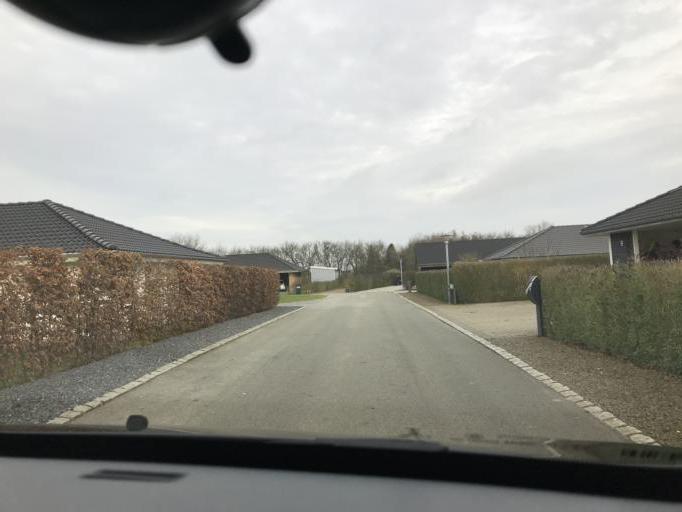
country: DK
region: South Denmark
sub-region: Faaborg-Midtfyn Kommune
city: Ringe
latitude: 55.2481
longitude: 10.4693
